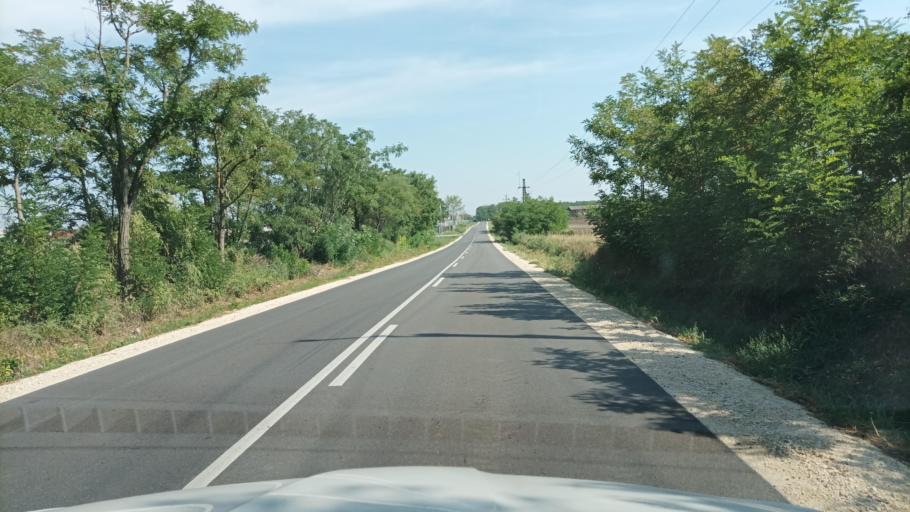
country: HU
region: Pest
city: Galgaheviz
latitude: 47.5916
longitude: 19.5737
